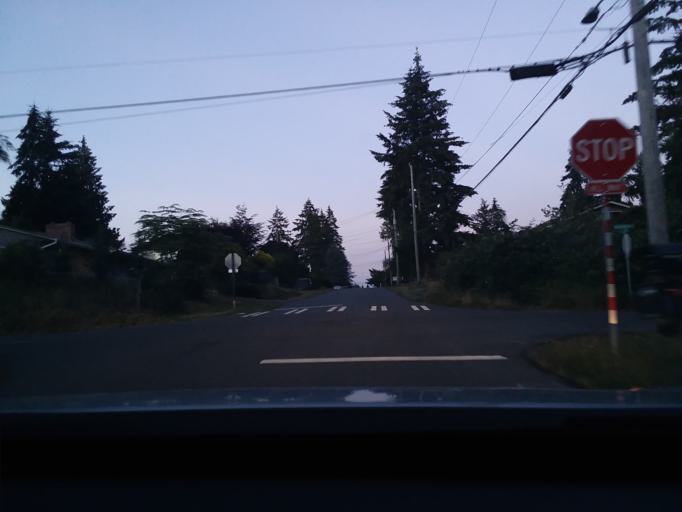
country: US
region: Washington
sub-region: King County
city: Shoreline
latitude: 47.7506
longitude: -122.3376
